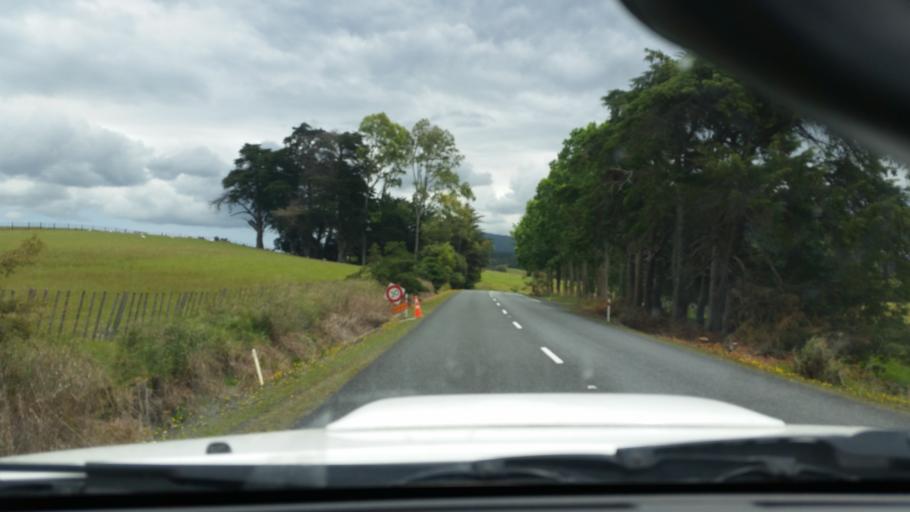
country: NZ
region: Northland
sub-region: Kaipara District
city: Dargaville
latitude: -35.7503
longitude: 173.8898
